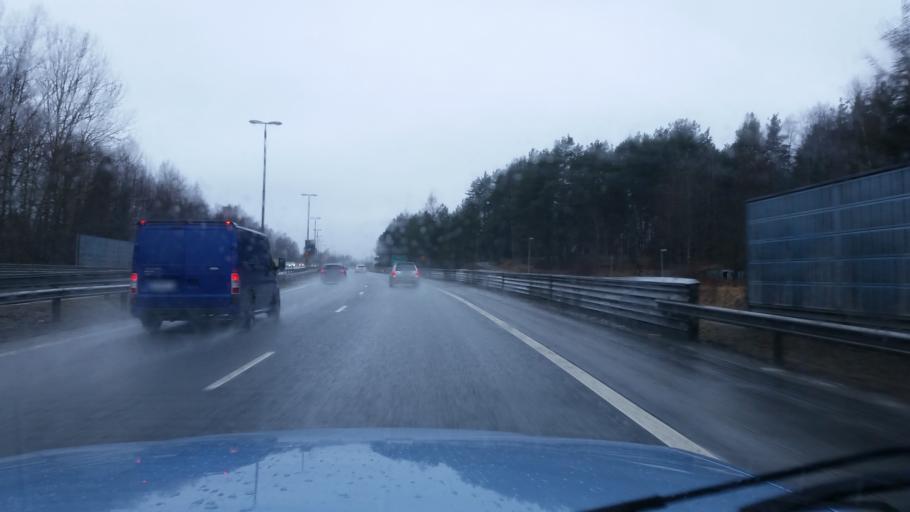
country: FI
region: Haeme
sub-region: Haemeenlinna
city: Haemeenlinna
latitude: 61.0030
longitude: 24.4471
